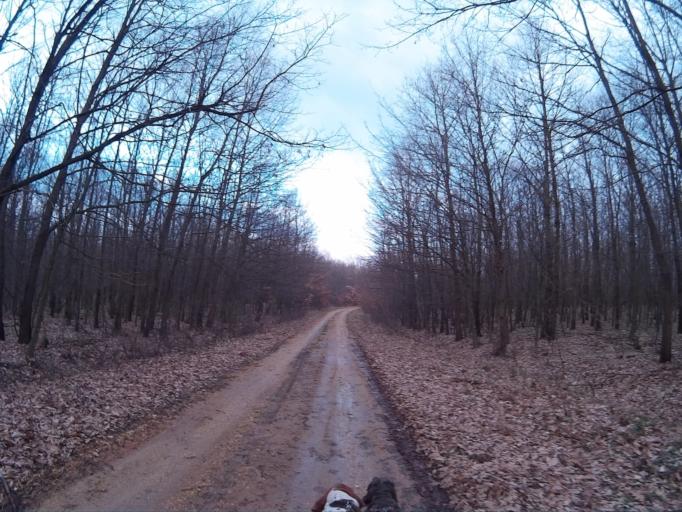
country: HU
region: Vas
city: Janoshaza
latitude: 47.1216
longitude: 17.0275
